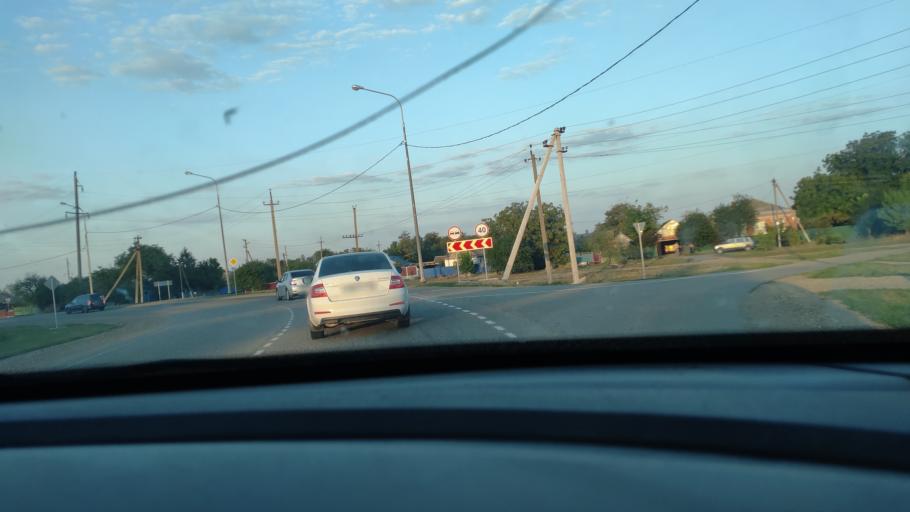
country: RU
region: Krasnodarskiy
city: Novominskaya
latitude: 46.3265
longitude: 38.9446
